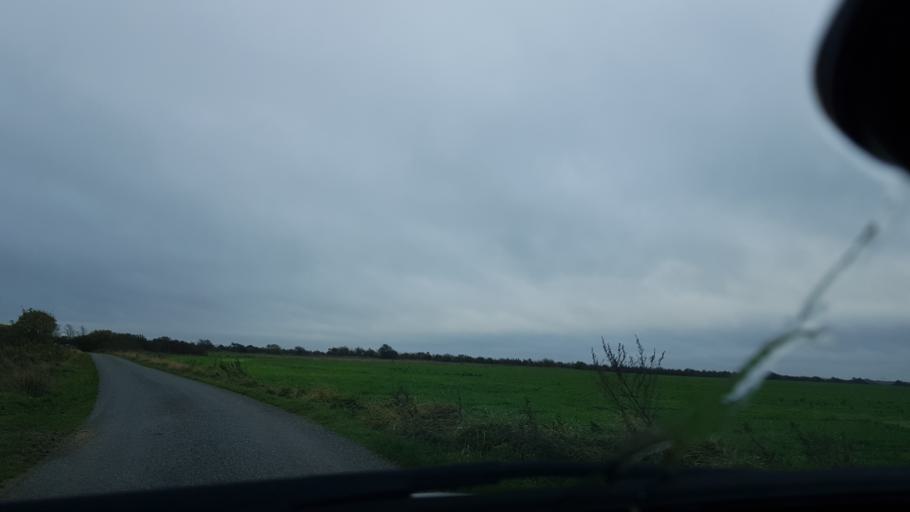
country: DK
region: South Denmark
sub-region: Esbjerg Kommune
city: Ribe
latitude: 55.2560
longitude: 8.8296
